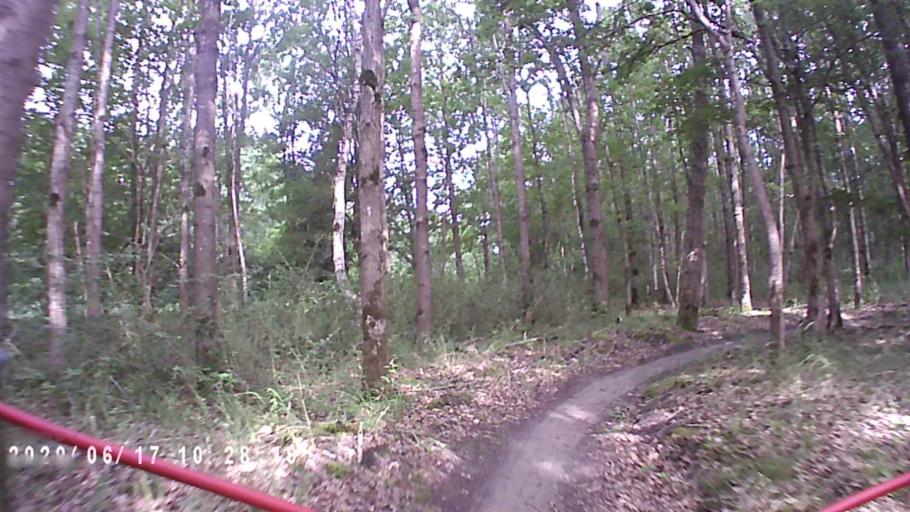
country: NL
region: Groningen
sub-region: Gemeente De Marne
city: Ulrum
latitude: 53.3956
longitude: 6.2414
